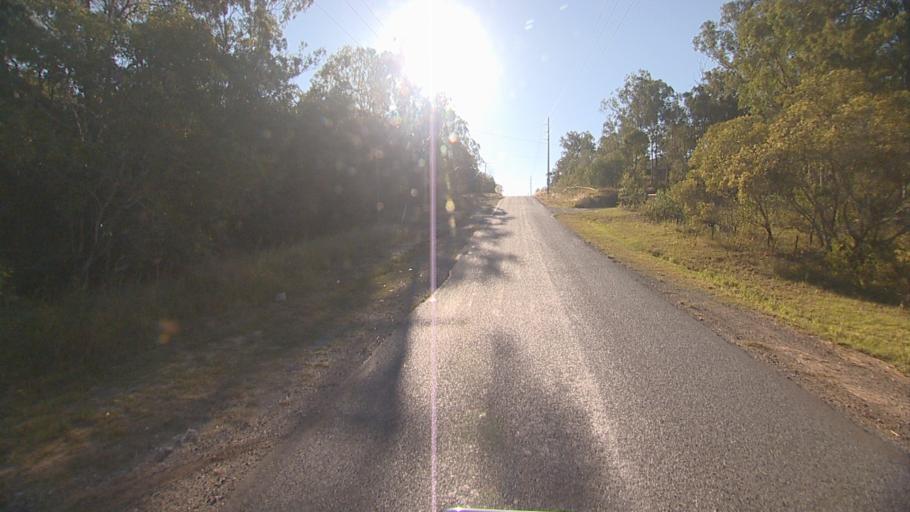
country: AU
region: Queensland
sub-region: Logan
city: North Maclean
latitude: -27.8075
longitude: 153.0434
